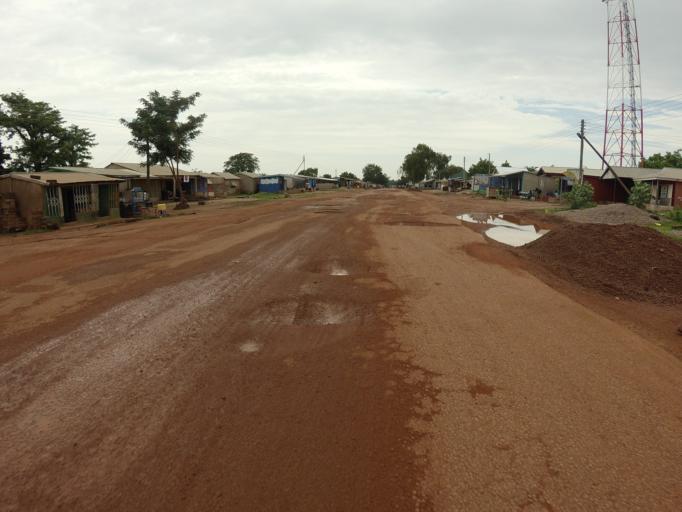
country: GH
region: Upper East
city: Bawku
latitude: 10.9369
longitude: -0.4922
